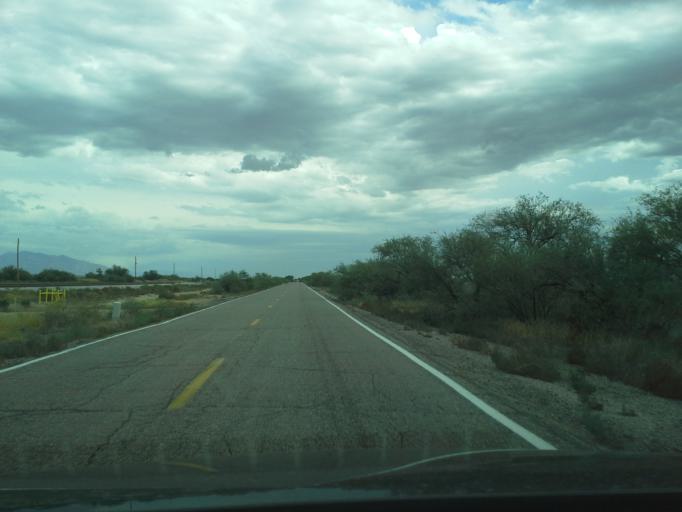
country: US
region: Arizona
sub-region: Pima County
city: Marana
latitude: 32.4831
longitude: -111.2447
